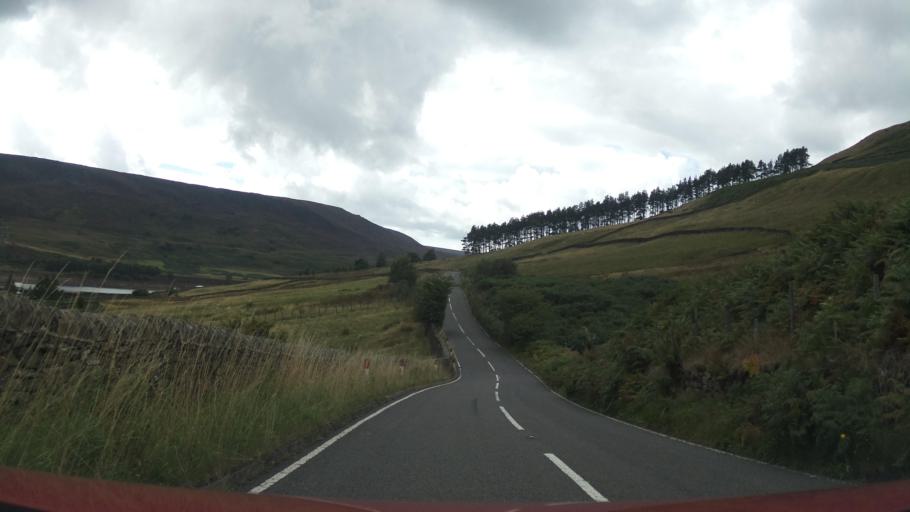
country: GB
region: England
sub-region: Kirklees
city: Meltham
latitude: 53.5006
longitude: -1.8594
